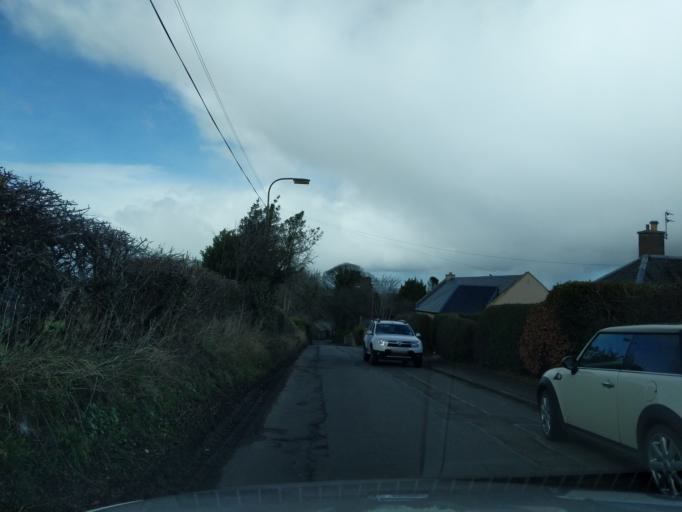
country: GB
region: Scotland
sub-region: Edinburgh
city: Currie
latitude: 55.8938
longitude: -3.3074
